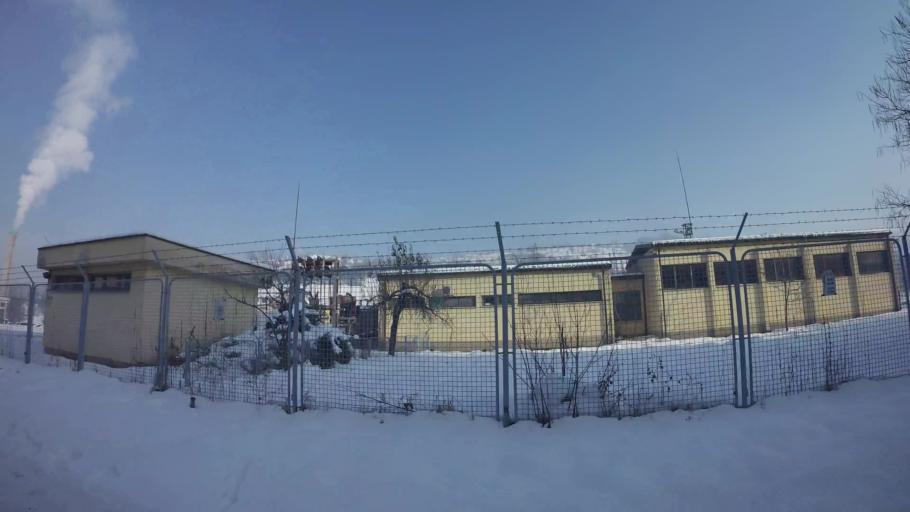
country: BA
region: Federation of Bosnia and Herzegovina
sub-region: Kanton Sarajevo
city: Sarajevo
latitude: 43.8317
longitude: 18.3486
